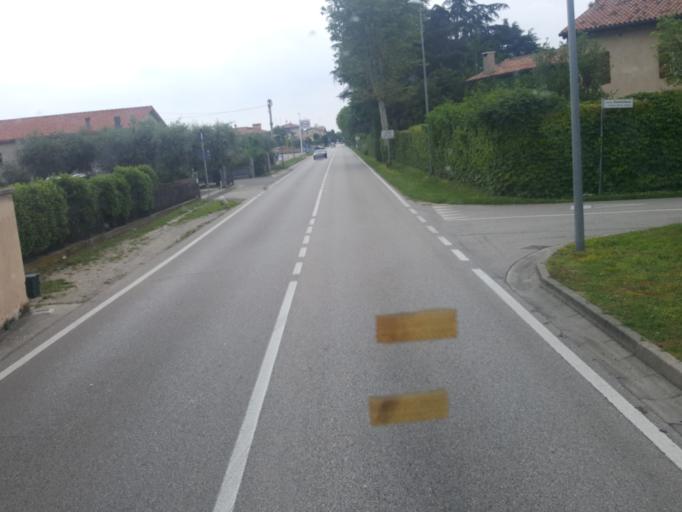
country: IT
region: Veneto
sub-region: Provincia di Vicenza
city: Pove del Grappa
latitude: 45.7871
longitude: 11.7346
